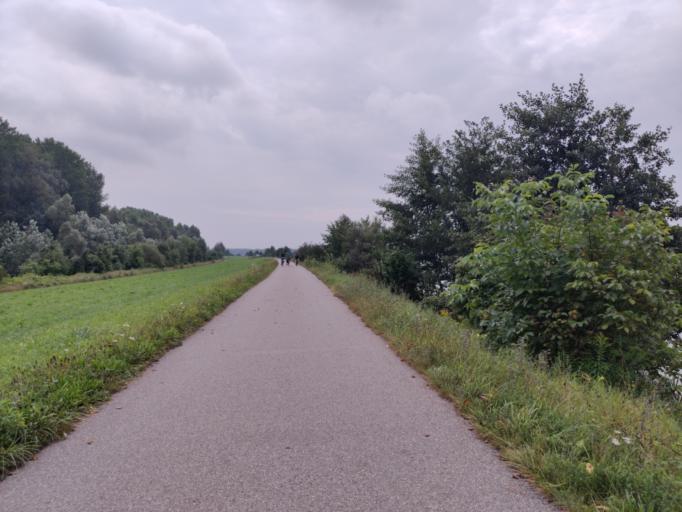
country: AT
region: Upper Austria
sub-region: Politischer Bezirk Urfahr-Umgebung
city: Steyregg
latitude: 48.2789
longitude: 14.3530
